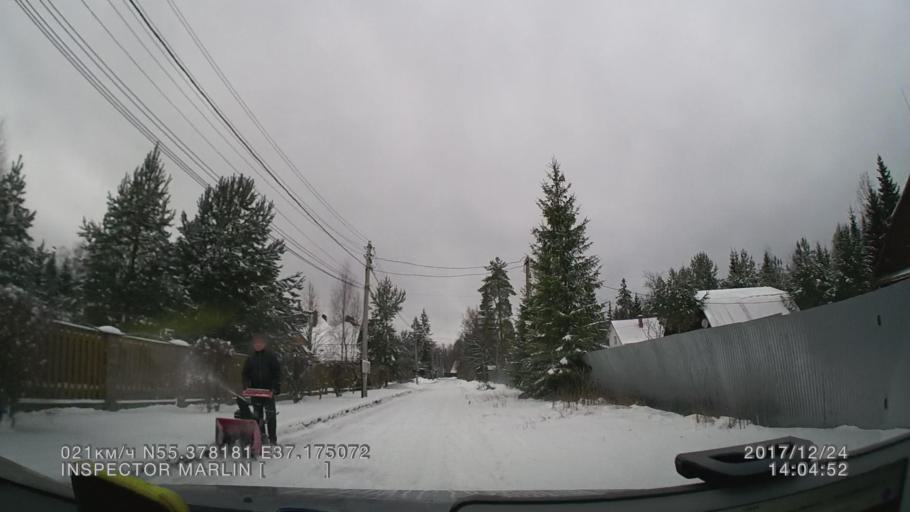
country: RU
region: Moskovskaya
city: Troitsk
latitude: 55.3782
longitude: 37.1750
